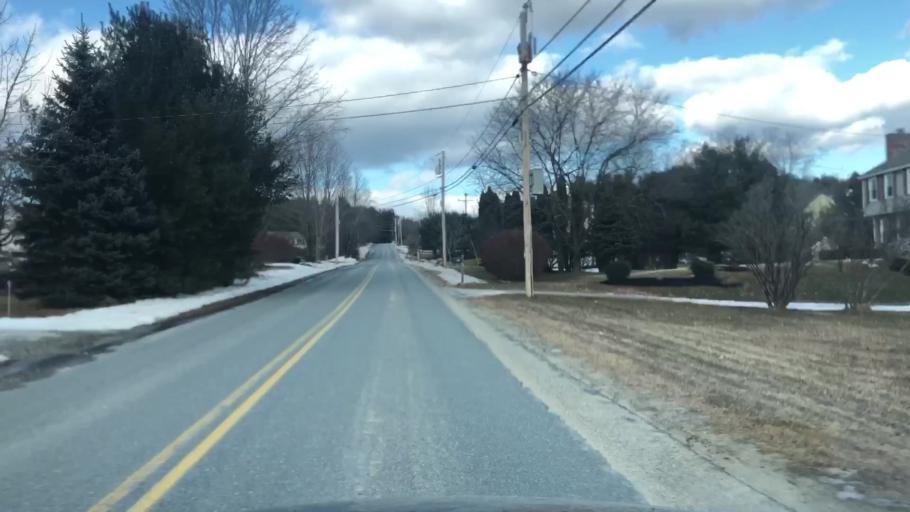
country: US
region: New Hampshire
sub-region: Hillsborough County
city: Milford
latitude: 42.8534
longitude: -71.6731
